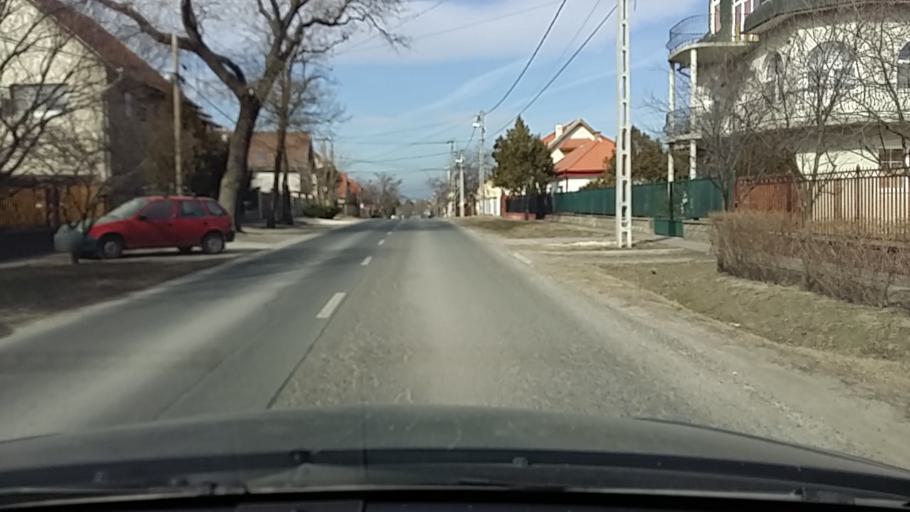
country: HU
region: Budapest
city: Budapest XXIII. keruelet
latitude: 47.3938
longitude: 19.0937
